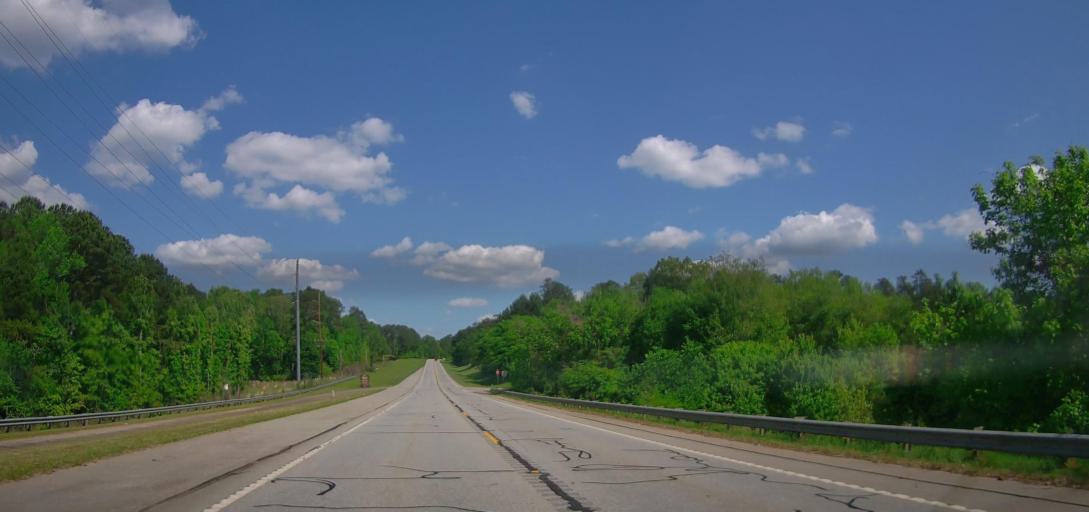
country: US
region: Georgia
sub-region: Greene County
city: Greensboro
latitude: 33.5806
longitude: -83.2714
